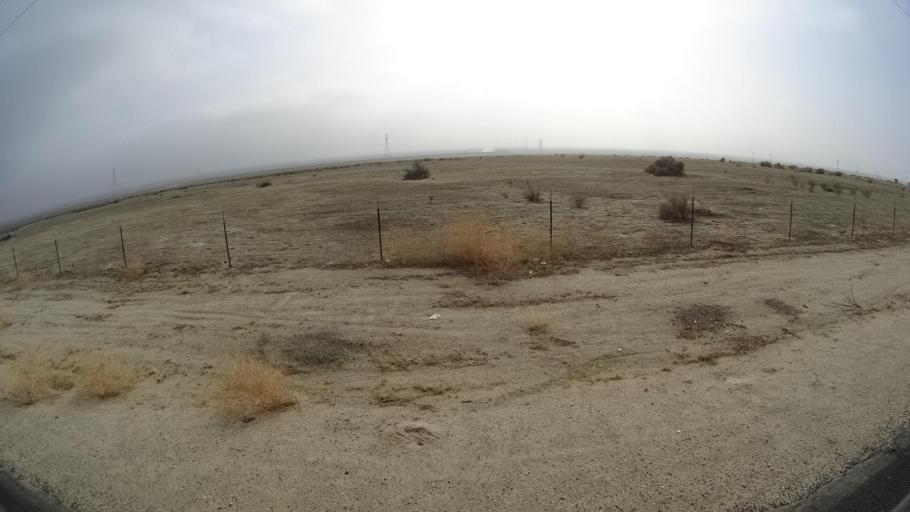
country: US
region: California
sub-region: Kern County
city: Ford City
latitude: 35.2329
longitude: -119.3559
